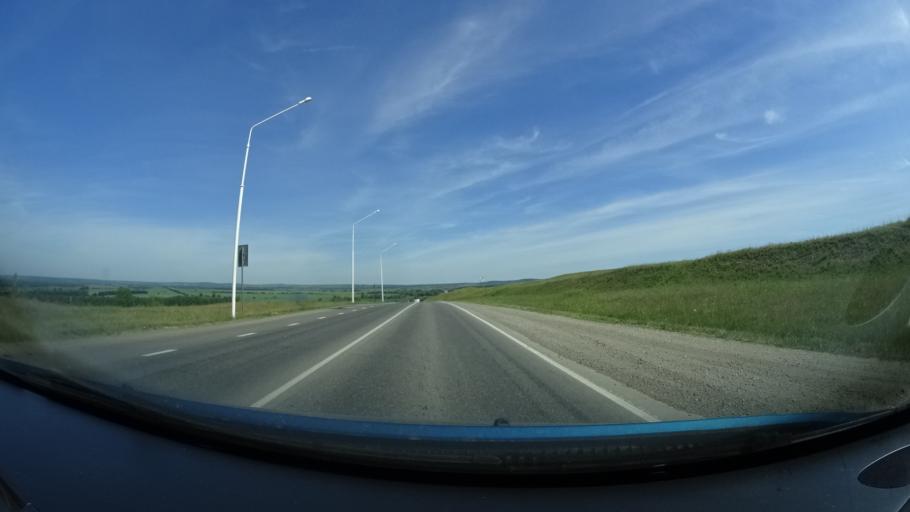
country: RU
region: Bashkortostan
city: Blagoveshchensk
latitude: 55.1772
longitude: 55.8537
